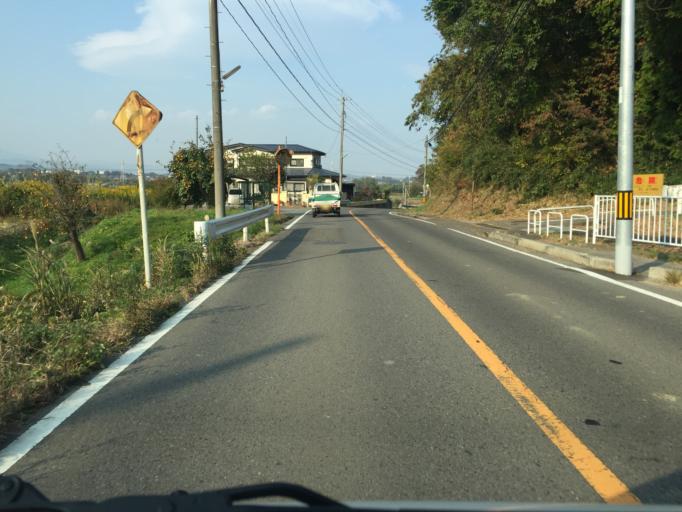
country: JP
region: Fukushima
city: Motomiya
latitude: 37.4719
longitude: 140.3895
